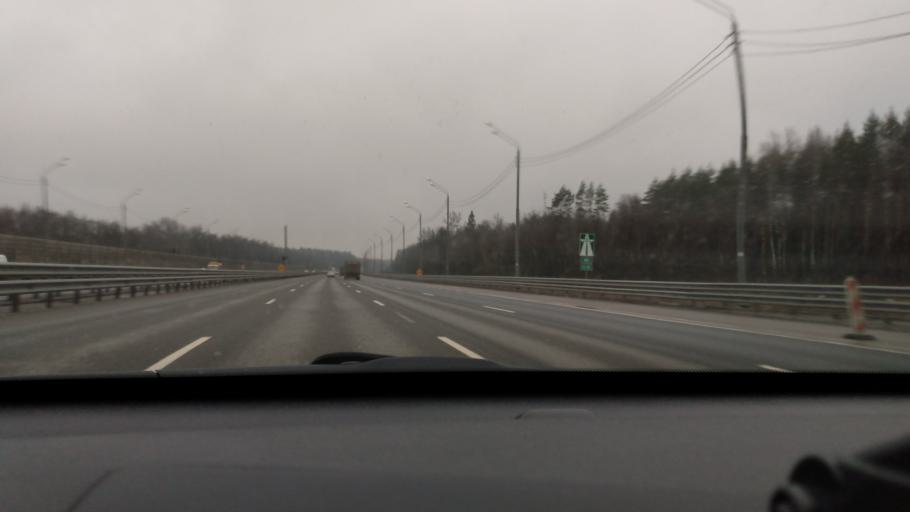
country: RU
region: Moskovskaya
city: Snegiri
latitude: 55.8189
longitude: 36.9624
